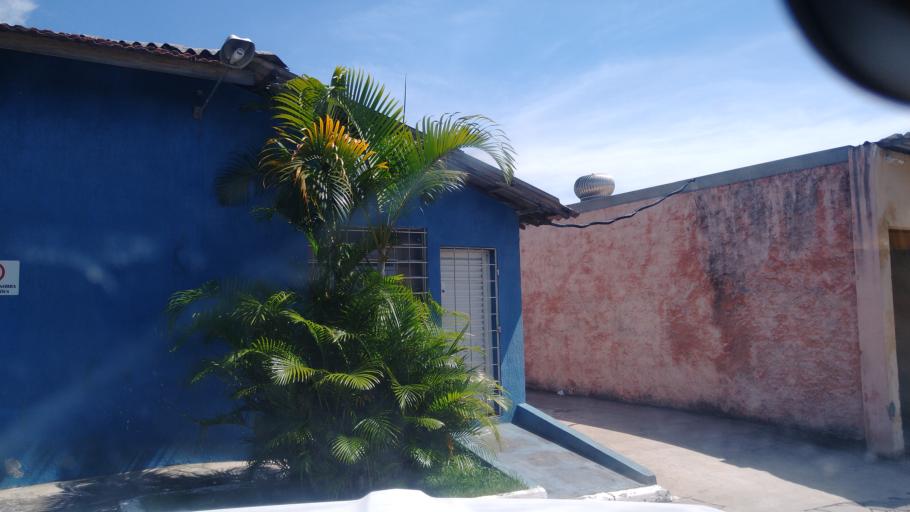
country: BR
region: Sao Paulo
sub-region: Guarulhos
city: Guarulhos
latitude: -23.4601
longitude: -46.5020
